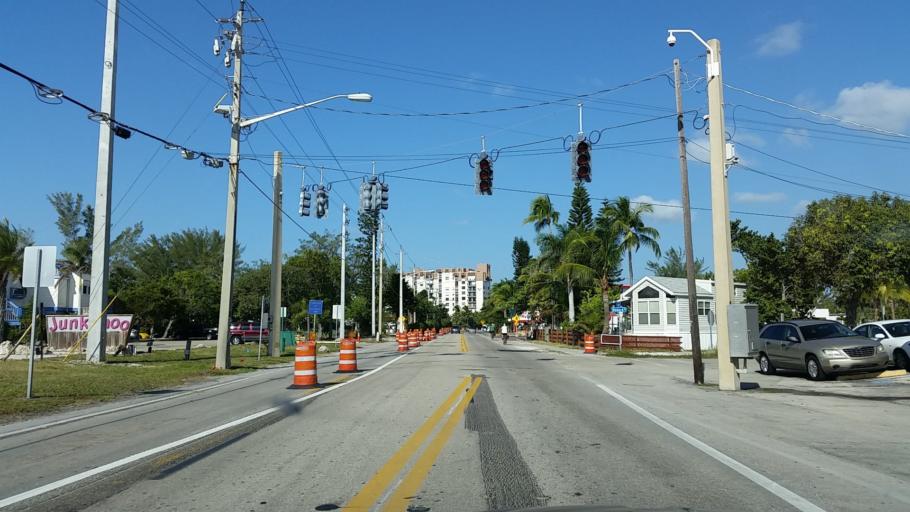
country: US
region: Florida
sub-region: Lee County
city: Fort Myers Beach
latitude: 26.4449
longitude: -81.9353
